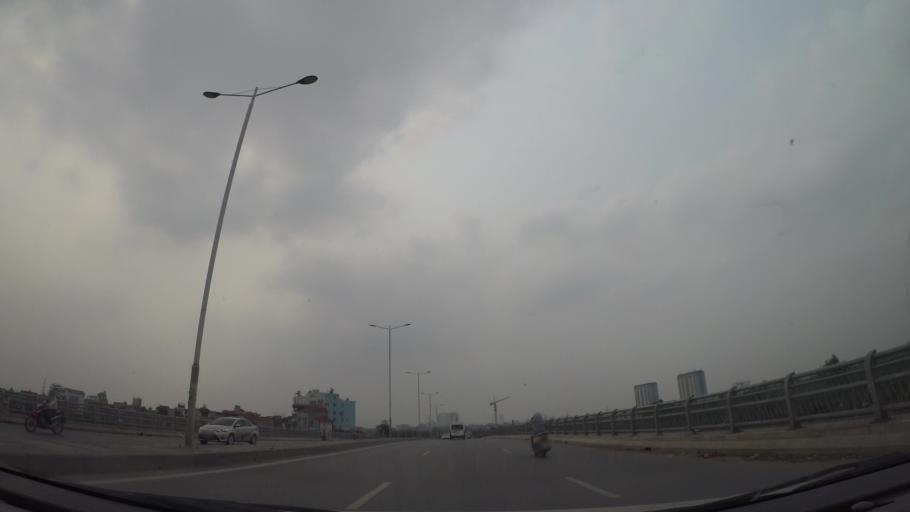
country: VN
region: Ha Noi
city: Cau Dien
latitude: 21.0342
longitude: 105.7524
